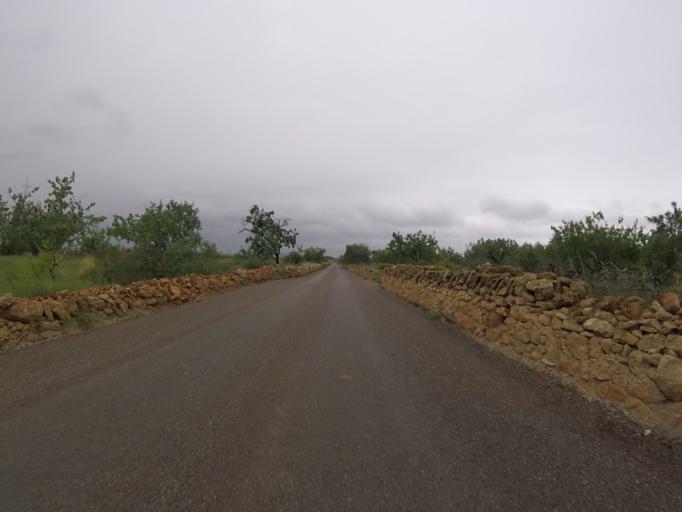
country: ES
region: Valencia
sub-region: Provincia de Castello
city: Alcoceber
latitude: 40.2363
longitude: 0.2542
